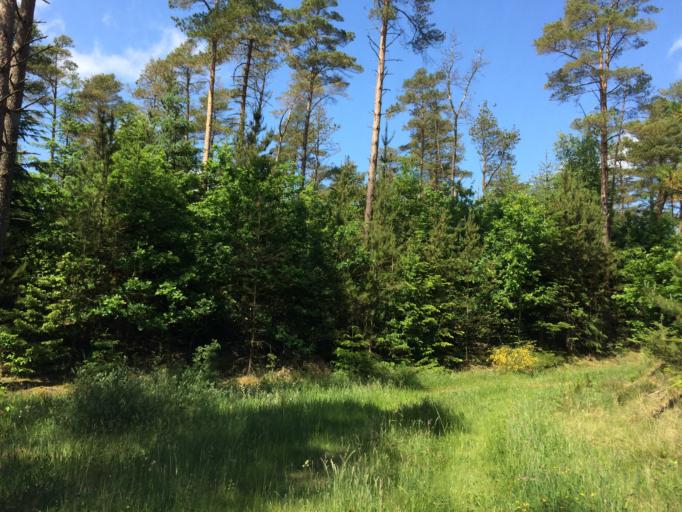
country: DK
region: Central Jutland
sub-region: Holstebro Kommune
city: Ulfborg
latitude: 56.2136
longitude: 8.4381
